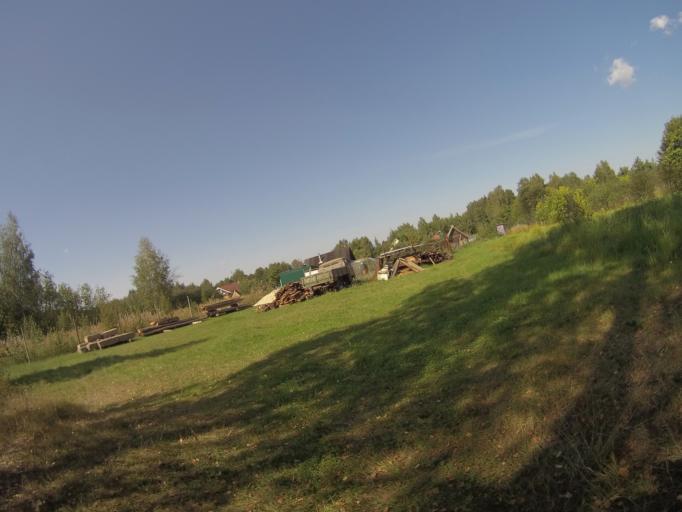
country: RU
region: Vladimir
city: Raduzhnyy
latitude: 55.9893
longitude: 40.2602
